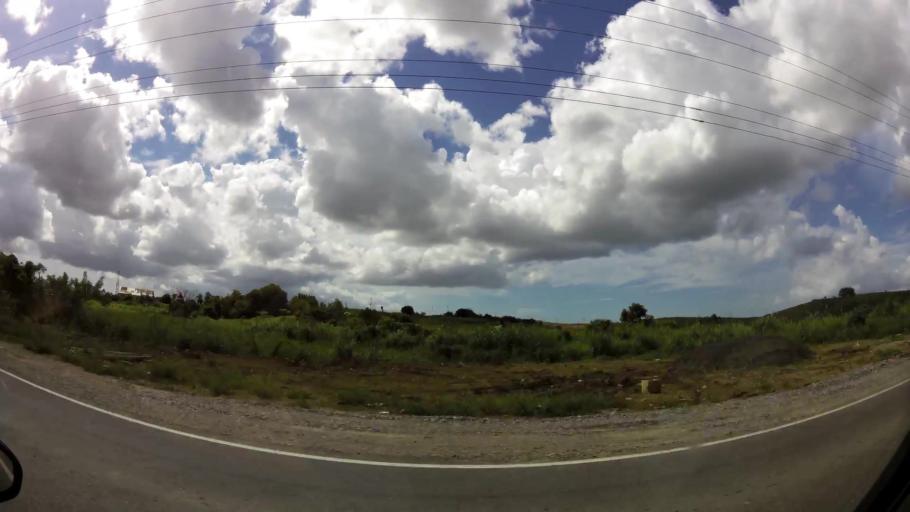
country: TT
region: Penal/Debe
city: Debe
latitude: 10.2261
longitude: -61.4819
